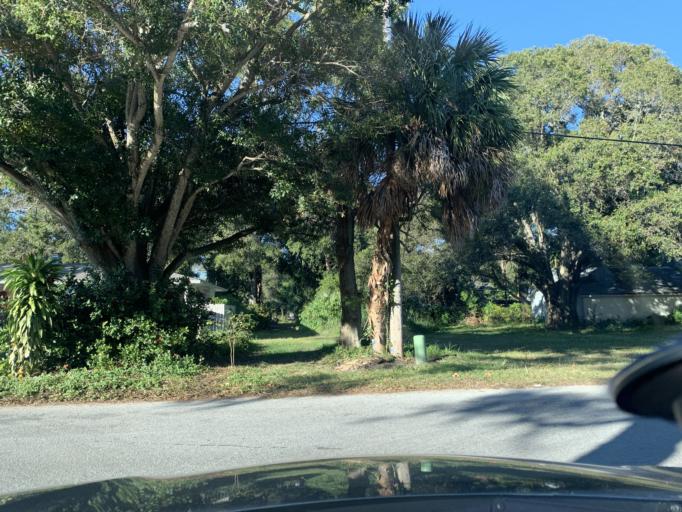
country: US
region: Florida
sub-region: Pinellas County
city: Gulfport
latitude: 27.7446
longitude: -82.7045
